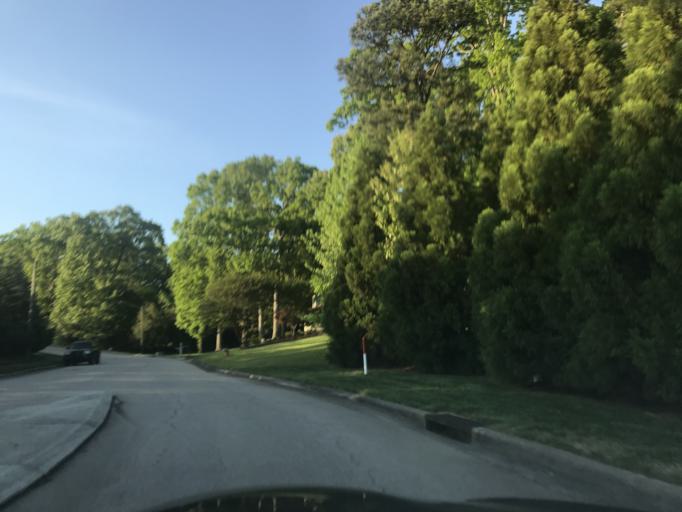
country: US
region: North Carolina
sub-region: Wake County
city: West Raleigh
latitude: 35.8975
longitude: -78.6062
